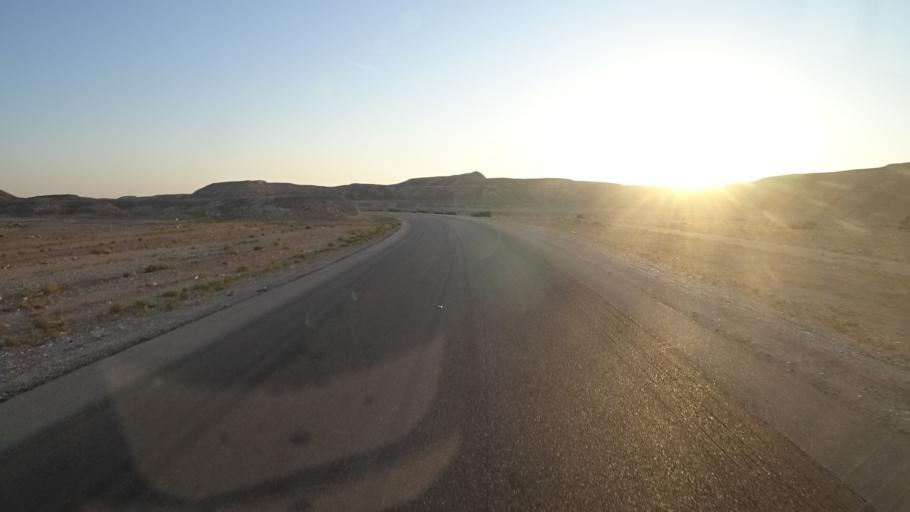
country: OM
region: Zufar
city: Salalah
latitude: 17.5072
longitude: 53.3651
